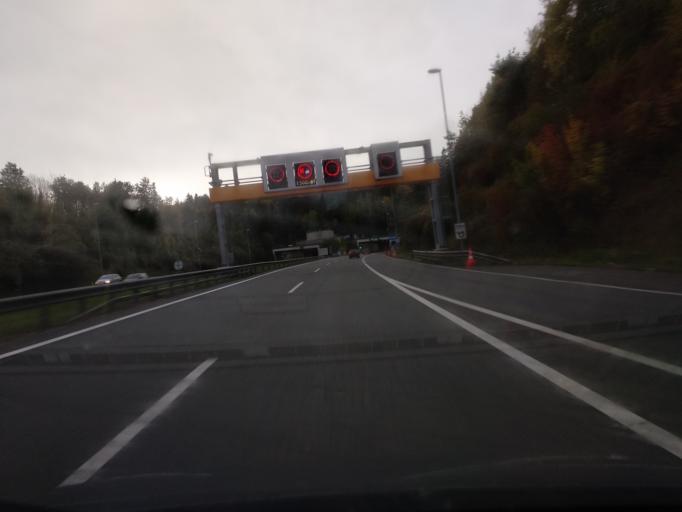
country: AT
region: Vorarlberg
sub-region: Politischer Bezirk Feldkirch
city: Feldkirch
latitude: 47.2303
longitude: 9.6168
